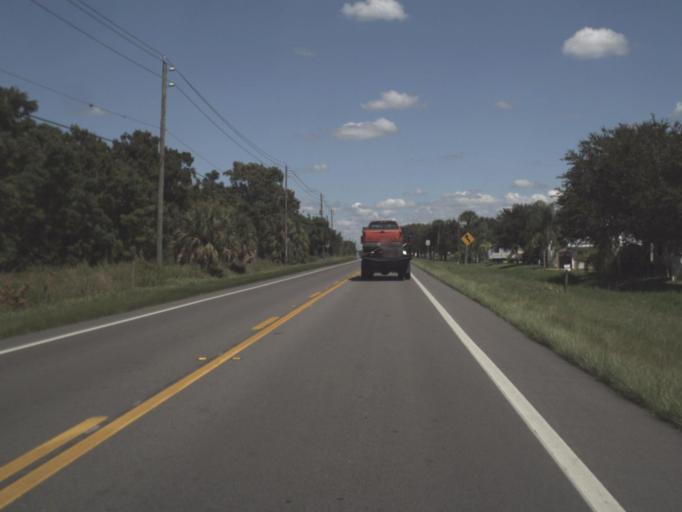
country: US
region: Florida
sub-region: Glades County
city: Buckhead Ridge
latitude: 27.1655
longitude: -80.8609
